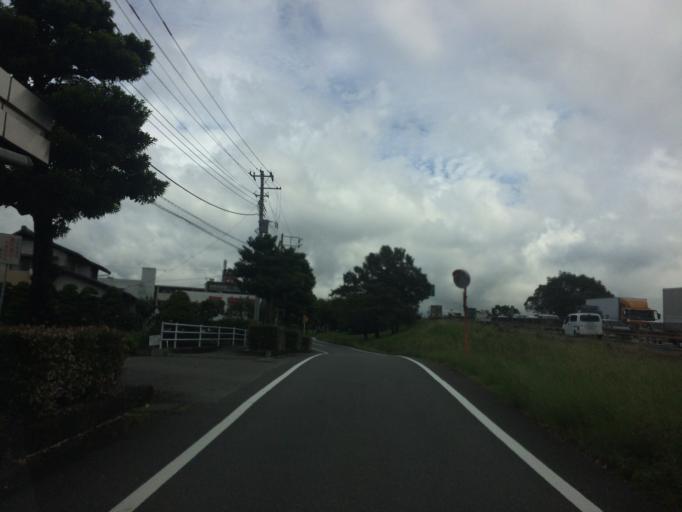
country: JP
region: Shizuoka
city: Fuji
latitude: 35.1713
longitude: 138.6726
